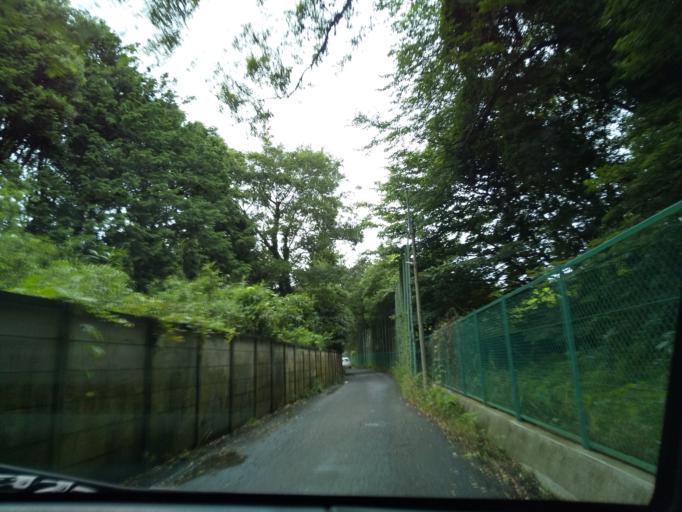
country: JP
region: Kanagawa
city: Minami-rinkan
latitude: 35.4263
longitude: 139.4434
